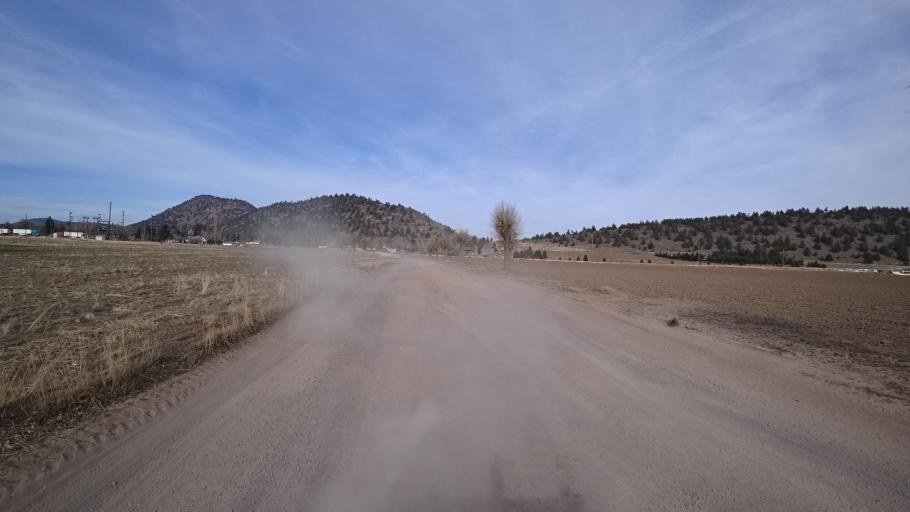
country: US
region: Oregon
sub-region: Klamath County
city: Klamath Falls
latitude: 41.9651
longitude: -121.9114
